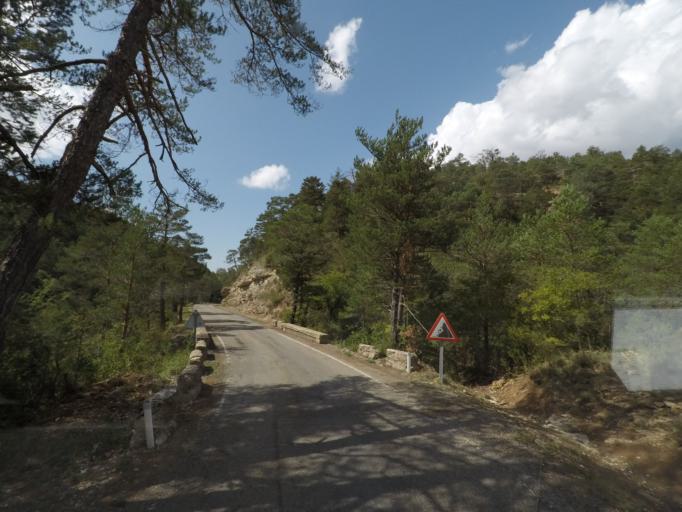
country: ES
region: Aragon
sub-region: Provincia de Huesca
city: Yebra de Basa
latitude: 42.4085
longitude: -0.2097
